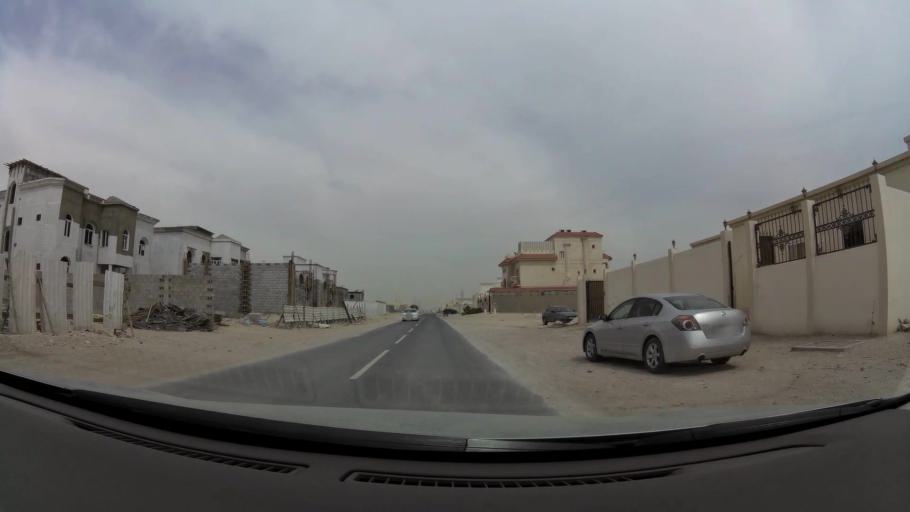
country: QA
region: Baladiyat ar Rayyan
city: Ar Rayyan
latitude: 25.2186
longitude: 51.4632
